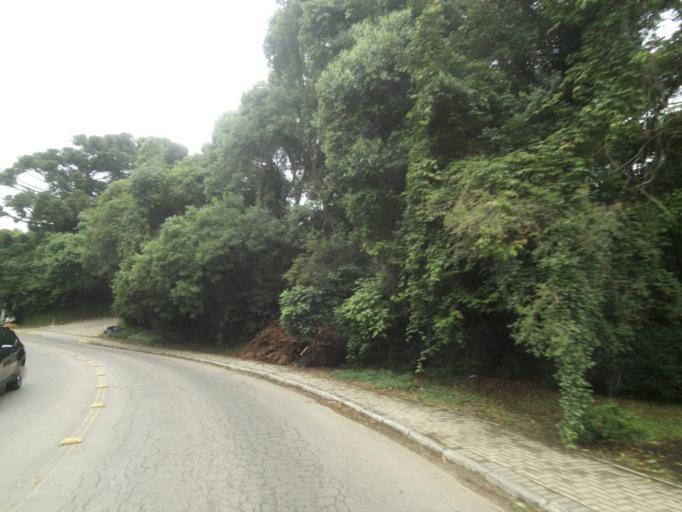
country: BR
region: Parana
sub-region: Curitiba
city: Curitiba
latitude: -25.4497
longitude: -49.3322
